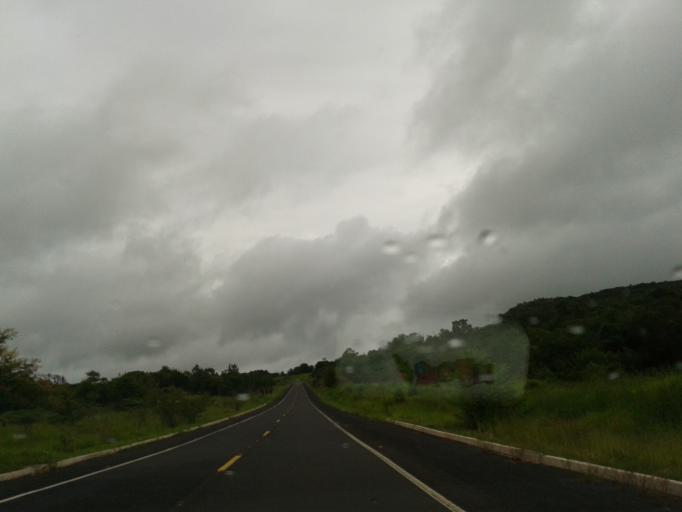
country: BR
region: Minas Gerais
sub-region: Santa Vitoria
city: Santa Vitoria
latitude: -19.2174
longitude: -50.0209
